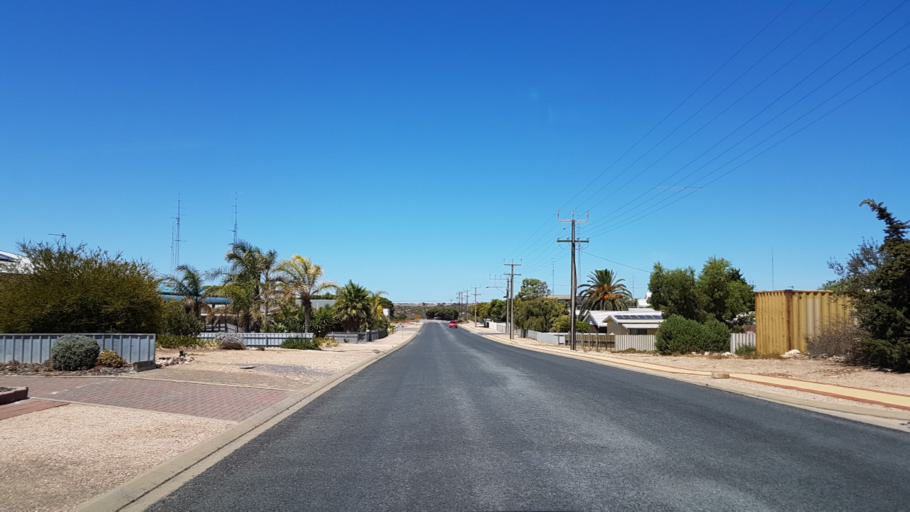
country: AU
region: South Australia
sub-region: Copper Coast
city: Wallaroo
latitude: -33.9047
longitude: 137.6325
